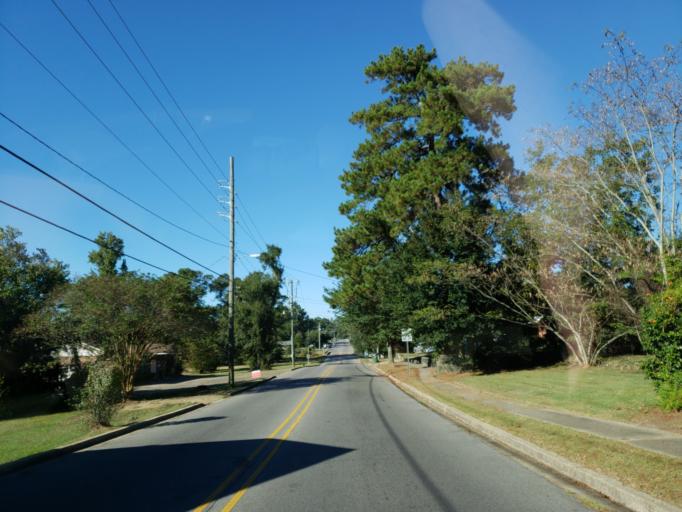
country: US
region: Mississippi
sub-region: Forrest County
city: Hattiesburg
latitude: 31.3259
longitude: -89.3100
